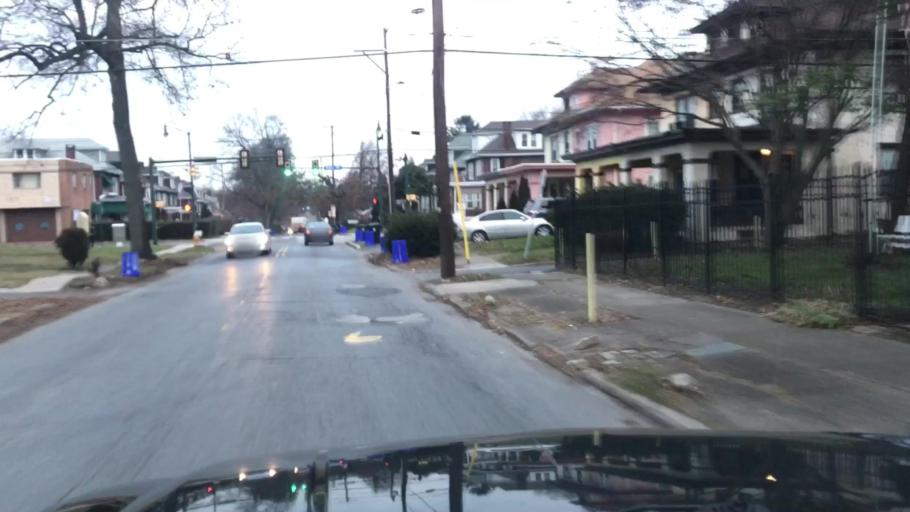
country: US
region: Pennsylvania
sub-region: Dauphin County
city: Harrisburg
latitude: 40.2751
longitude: -76.8685
